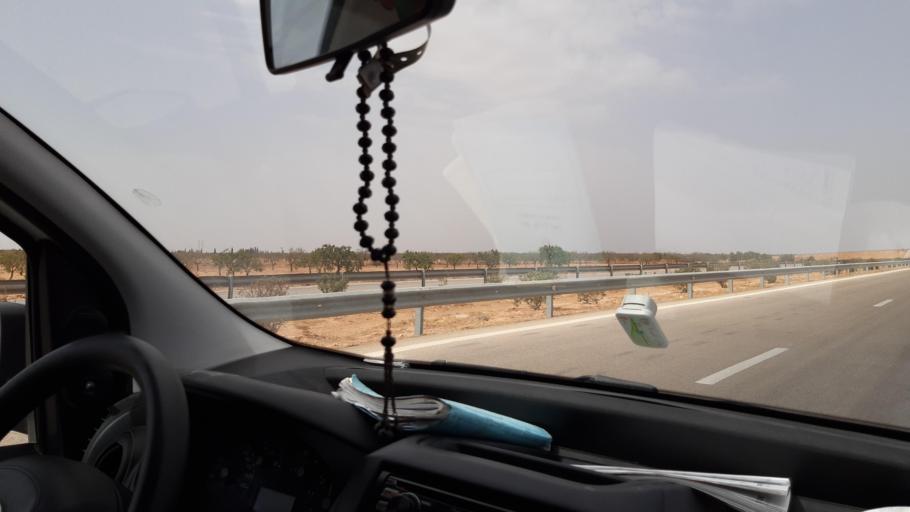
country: TN
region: Safaqis
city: Sfax
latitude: 34.8530
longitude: 10.6803
